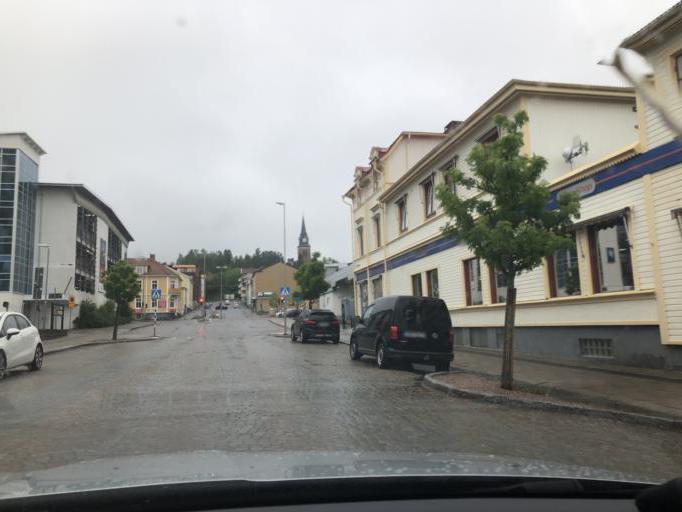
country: SE
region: Vaesternorrland
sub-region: OErnskoeldsviks Kommun
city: Ornskoldsvik
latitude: 63.2903
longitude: 18.7129
